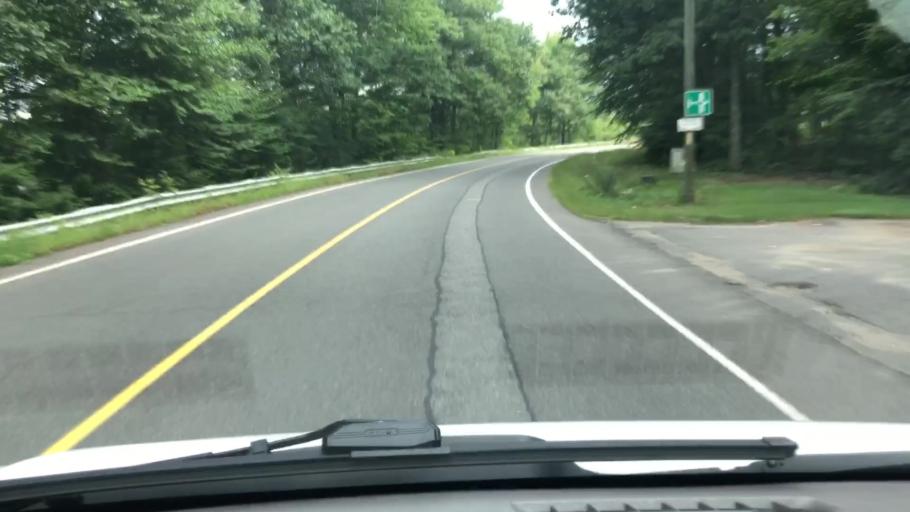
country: US
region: Massachusetts
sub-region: Franklin County
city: Turners Falls
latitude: 42.5946
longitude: -72.5295
